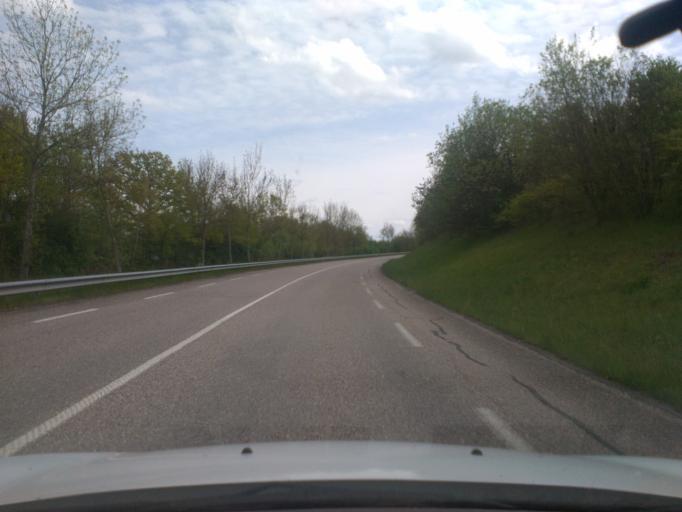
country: FR
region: Lorraine
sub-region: Departement des Vosges
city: Mirecourt
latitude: 48.2336
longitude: 6.2120
